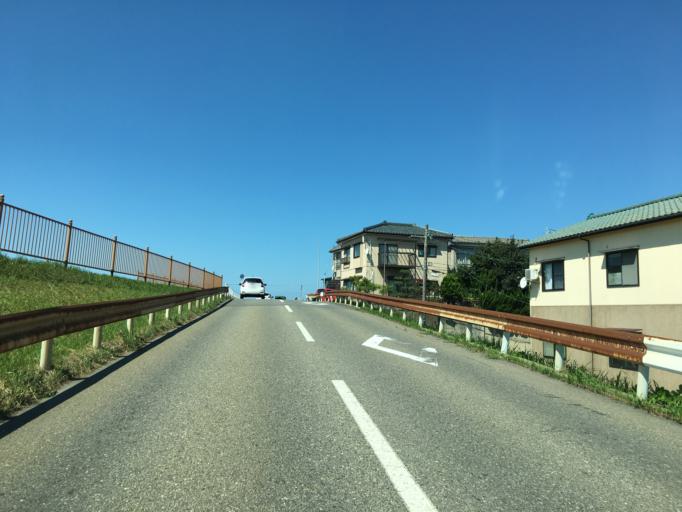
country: JP
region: Niigata
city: Niigata-shi
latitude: 37.9003
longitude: 139.0102
